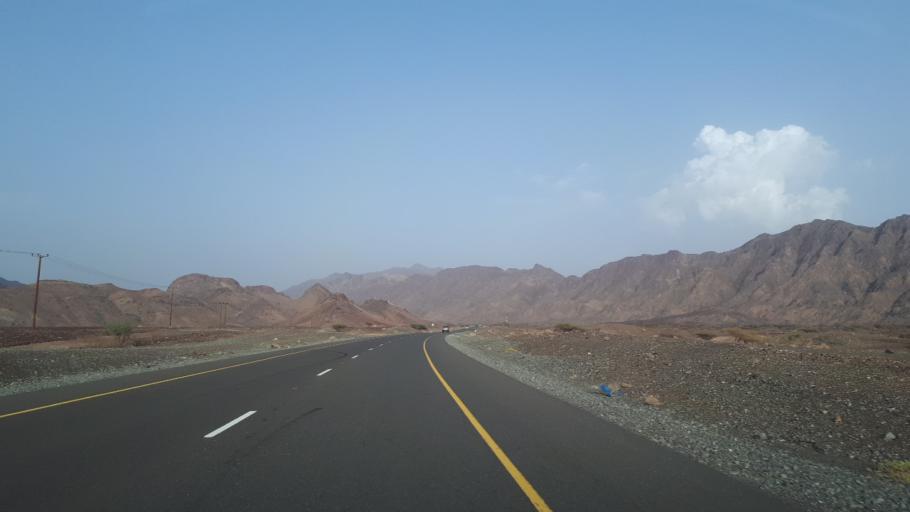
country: OM
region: Az Zahirah
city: Yanqul
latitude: 23.4968
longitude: 56.8542
